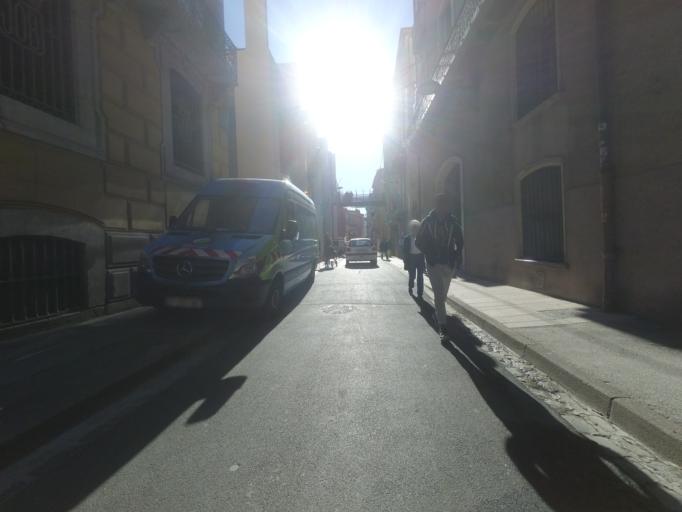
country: FR
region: Languedoc-Roussillon
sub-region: Departement des Pyrenees-Orientales
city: Perpignan
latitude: 42.6981
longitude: 2.8983
